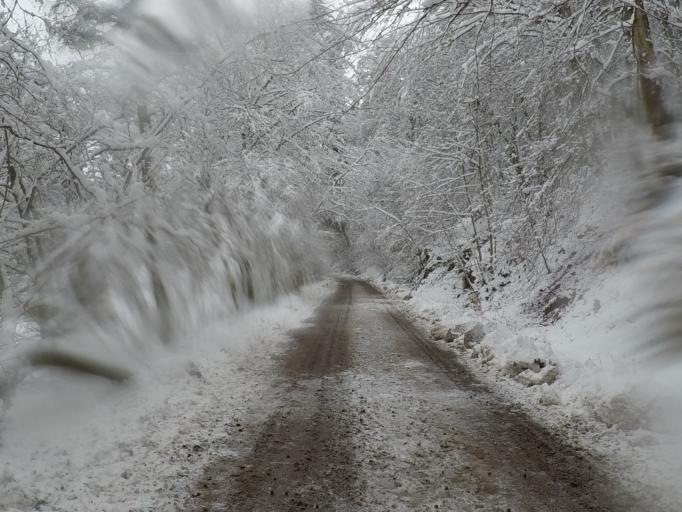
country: DE
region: North Rhine-Westphalia
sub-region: Regierungsbezirk Koln
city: Simmerath
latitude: 50.6516
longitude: 6.3212
